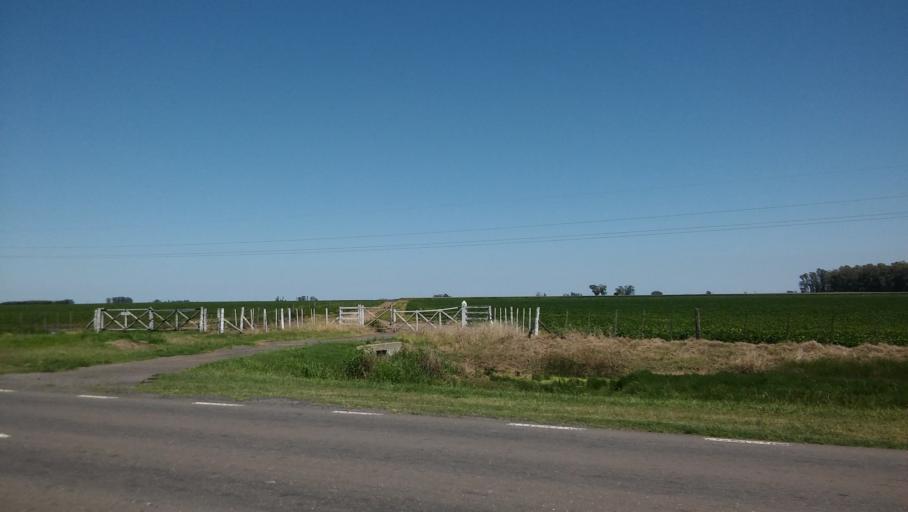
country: AR
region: Cordoba
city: Arias
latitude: -34.0312
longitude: -62.2942
